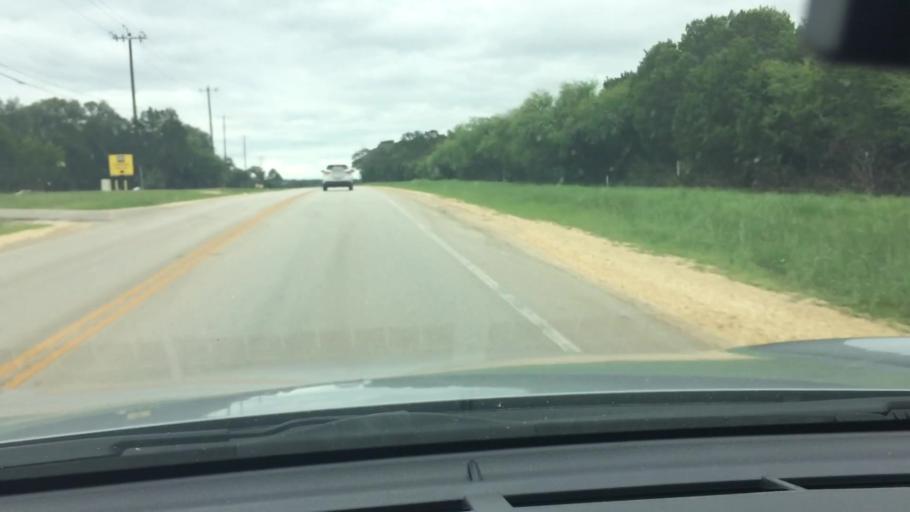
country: US
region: Texas
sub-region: Comal County
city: Garden Ridge
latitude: 29.6430
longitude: -98.3909
